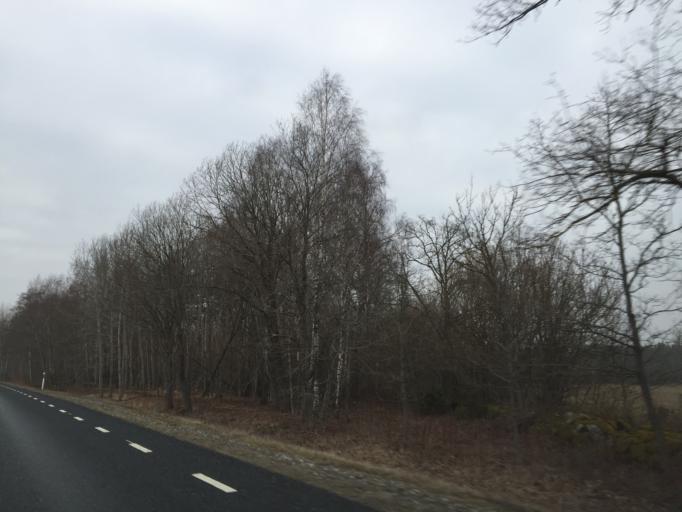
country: EE
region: Saare
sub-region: Orissaare vald
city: Orissaare
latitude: 58.6065
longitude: 23.2936
